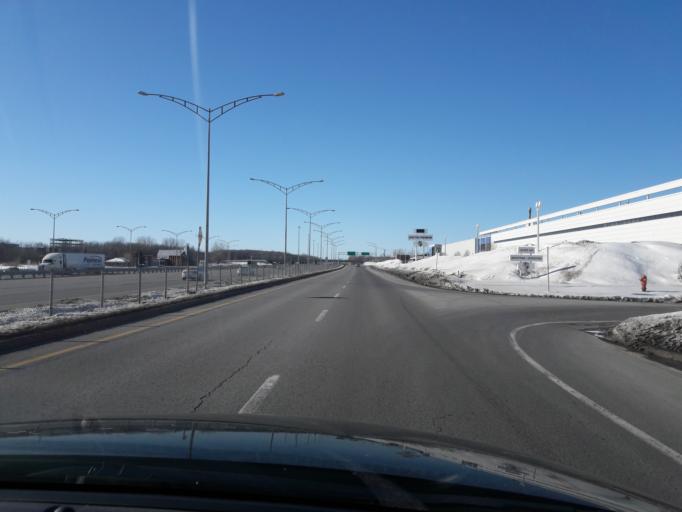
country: CA
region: Quebec
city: Dollard-Des Ormeaux
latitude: 45.5370
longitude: -73.7894
